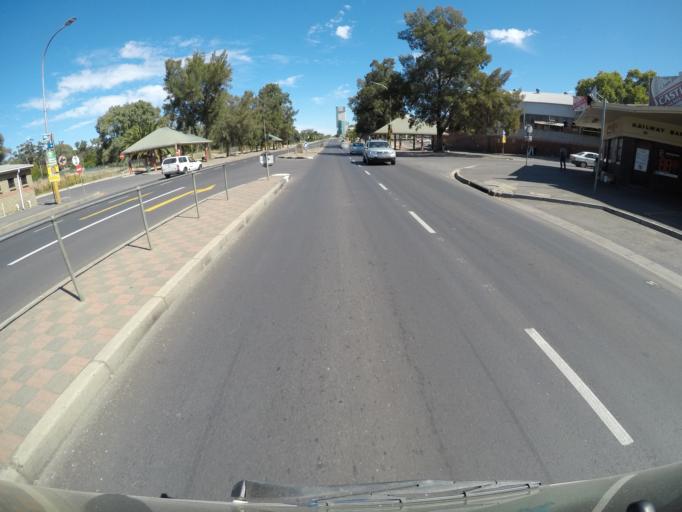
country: ZA
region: Western Cape
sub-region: West Coast District Municipality
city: Malmesbury
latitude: -33.4662
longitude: 18.7276
